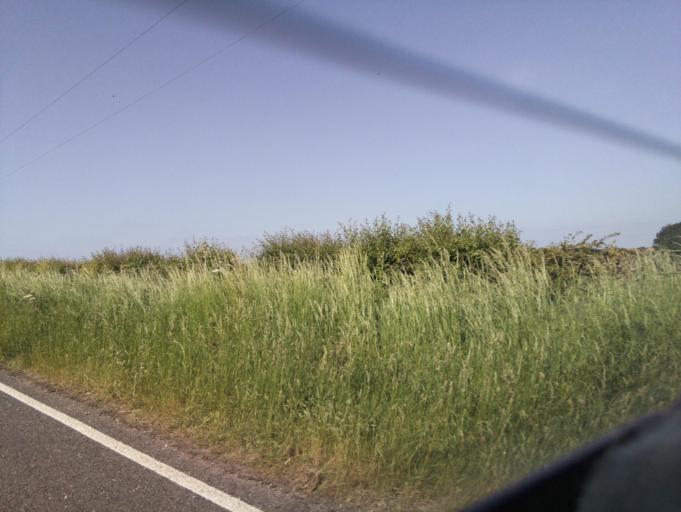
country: GB
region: England
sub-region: Hampshire
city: Kings Worthy
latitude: 51.1461
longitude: -1.3420
